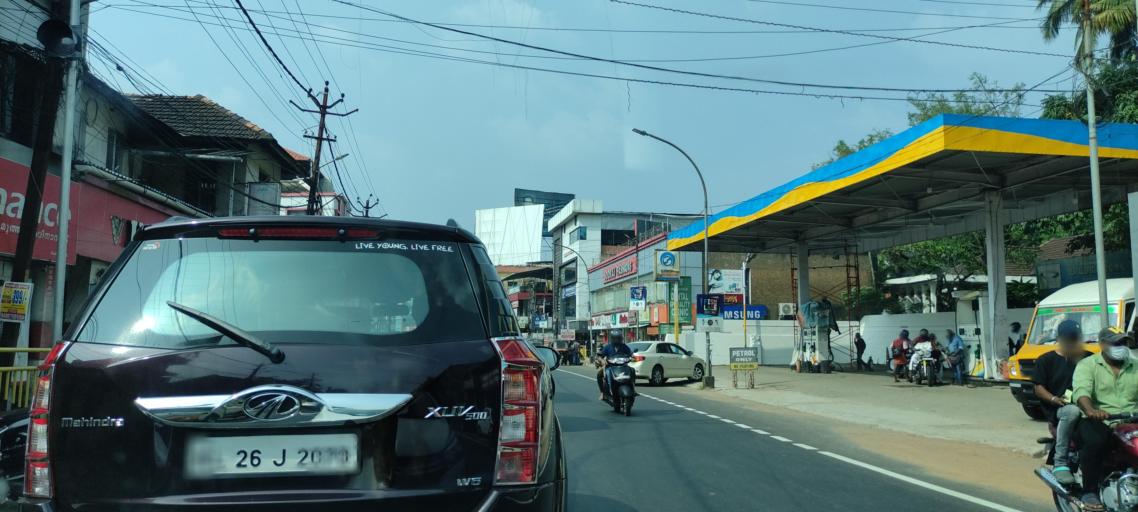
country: IN
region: Kerala
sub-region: Alappuzha
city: Chengannur
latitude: 9.3166
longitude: 76.6164
